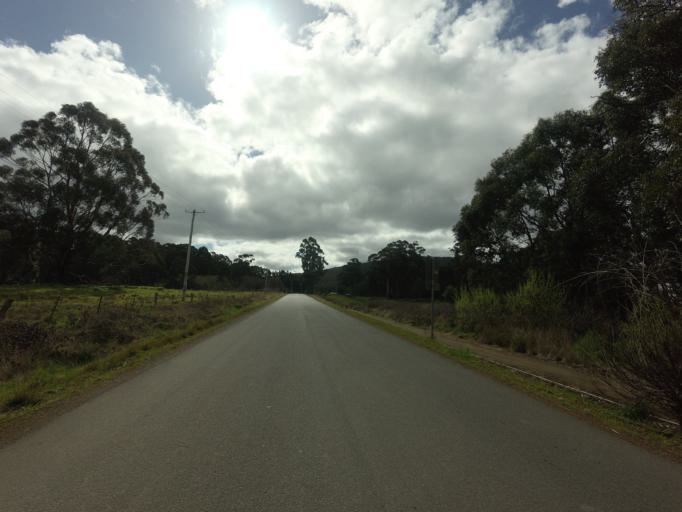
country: AU
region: Tasmania
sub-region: Huon Valley
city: Geeveston
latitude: -43.4300
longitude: 146.9739
